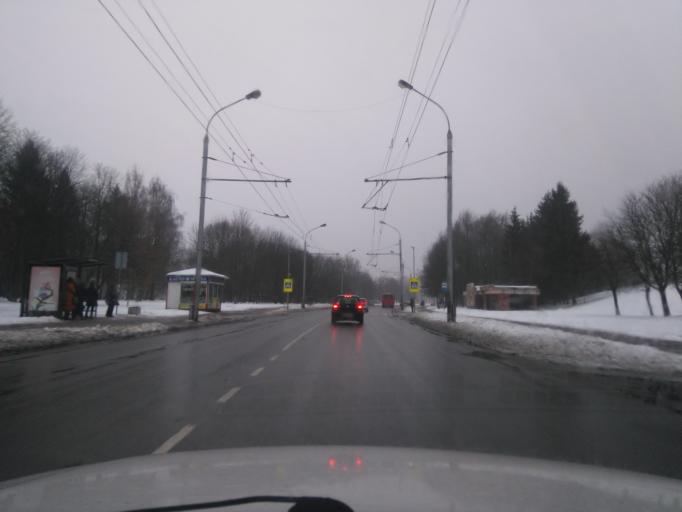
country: LT
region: Kauno apskritis
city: Dainava (Kaunas)
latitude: 54.9162
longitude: 23.9734
